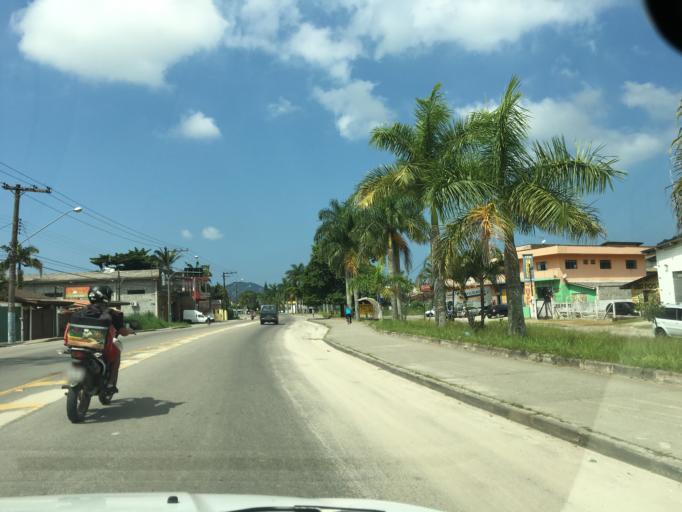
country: BR
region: Sao Paulo
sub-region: Ubatuba
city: Ubatuba
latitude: -23.4369
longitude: -45.0977
